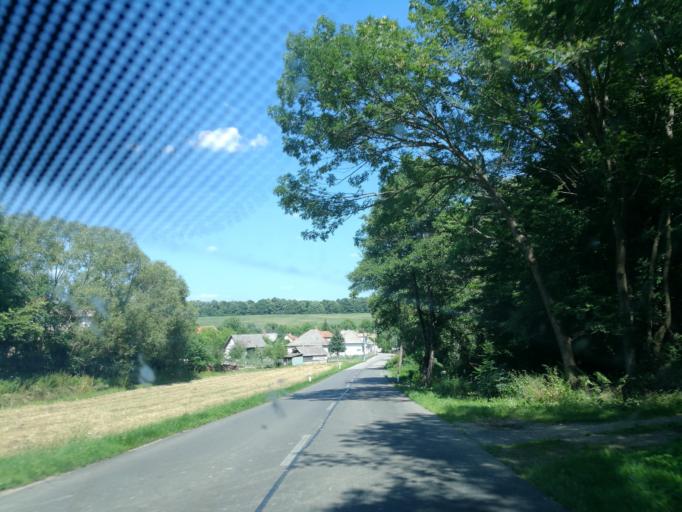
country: SK
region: Nitriansky
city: Banovce nad Bebravou
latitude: 48.7252
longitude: 18.1405
